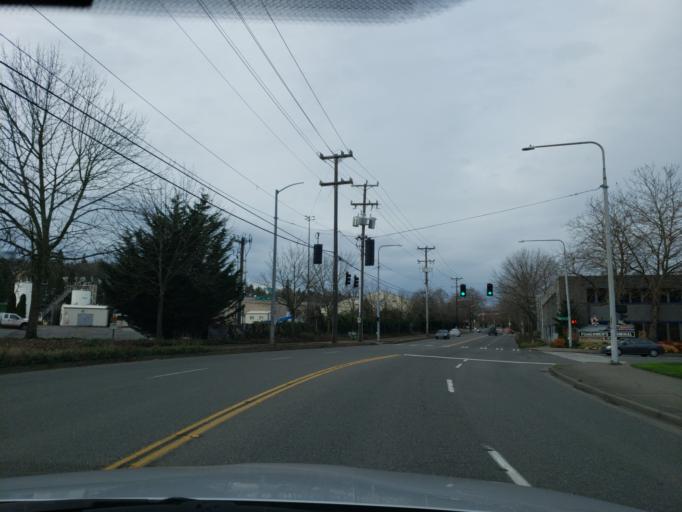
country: US
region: Washington
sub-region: King County
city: Seattle
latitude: 47.6541
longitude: -122.3809
